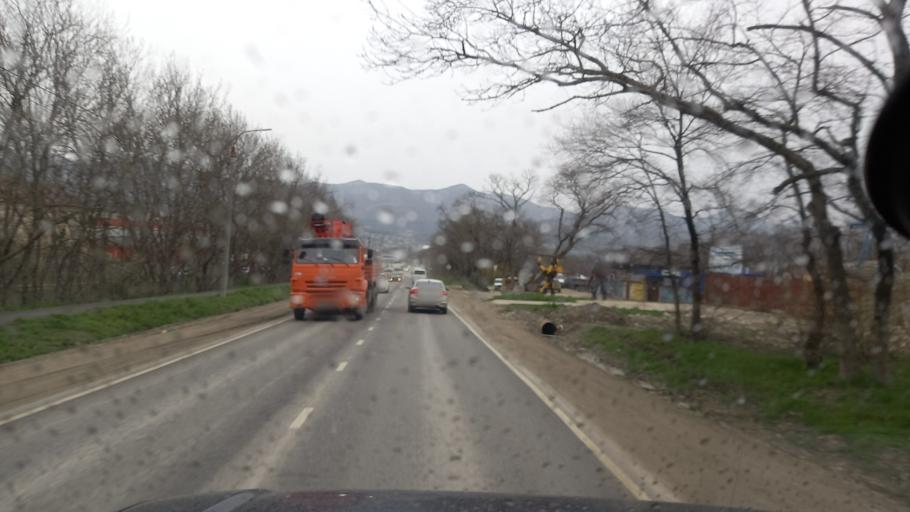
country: RU
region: Krasnodarskiy
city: Gayduk
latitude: 44.7561
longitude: 37.7062
